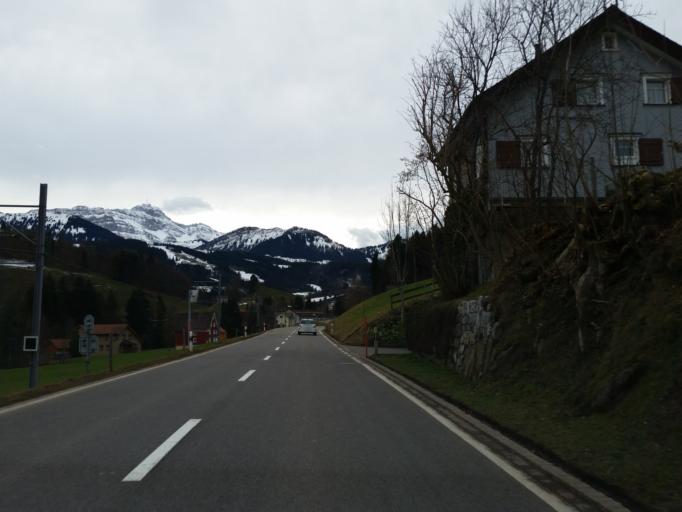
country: CH
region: Appenzell Ausserrhoden
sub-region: Bezirk Hinterland
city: Waldstatt
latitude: 47.3402
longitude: 9.2913
